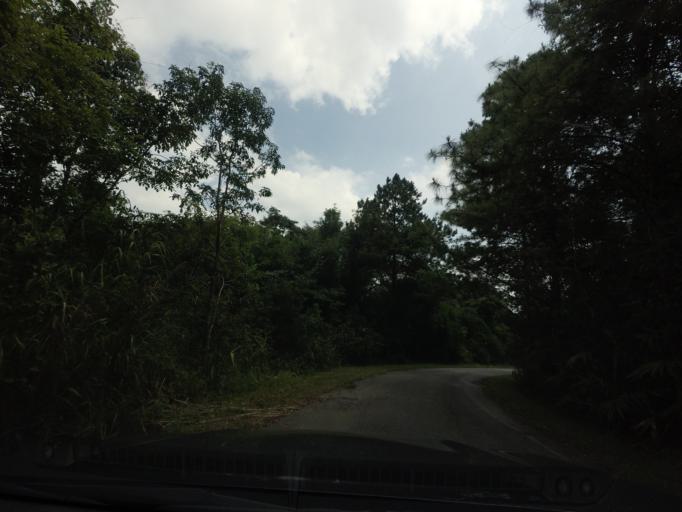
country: TH
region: Loei
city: Phu Ruea
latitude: 17.4883
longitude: 101.3532
